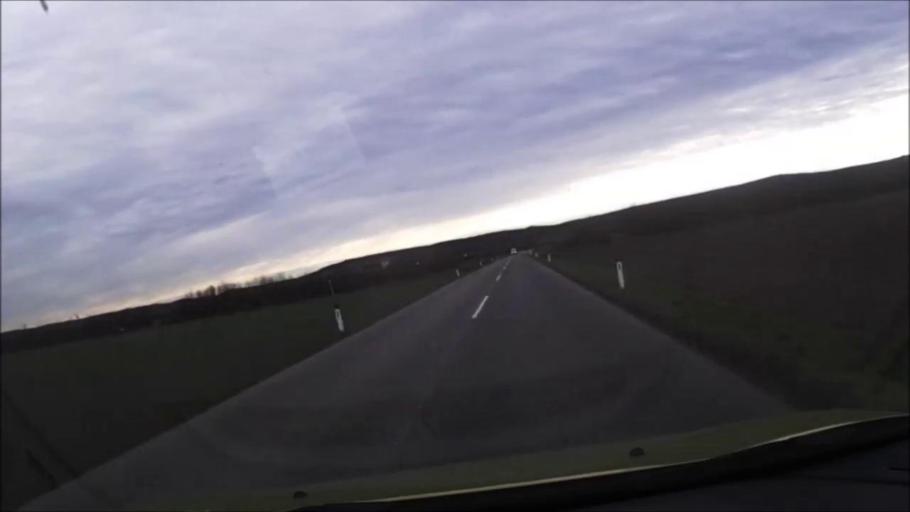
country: AT
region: Burgenland
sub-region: Eisenstadt-Umgebung
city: Leithaprodersdorf
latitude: 47.9268
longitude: 16.4993
